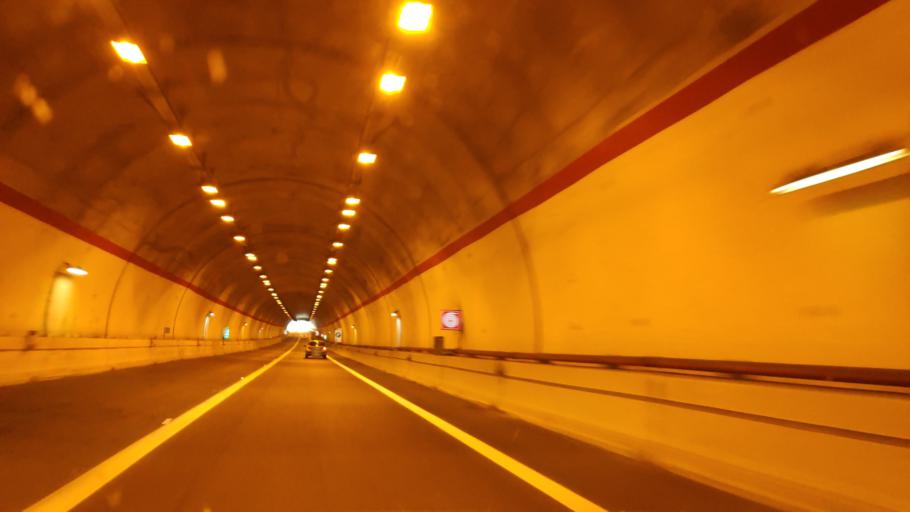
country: IT
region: Calabria
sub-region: Provincia di Reggio Calabria
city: Locri
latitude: 38.2408
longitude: 16.2415
